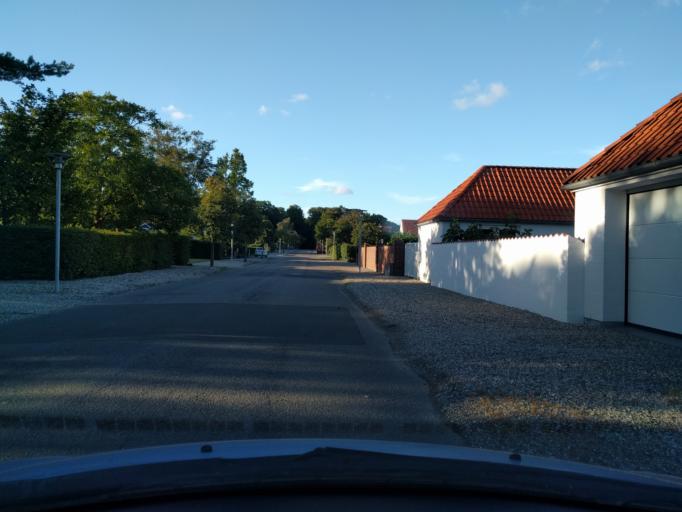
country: DK
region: South Denmark
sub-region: Nyborg Kommune
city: Nyborg
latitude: 55.3299
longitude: 10.8074
